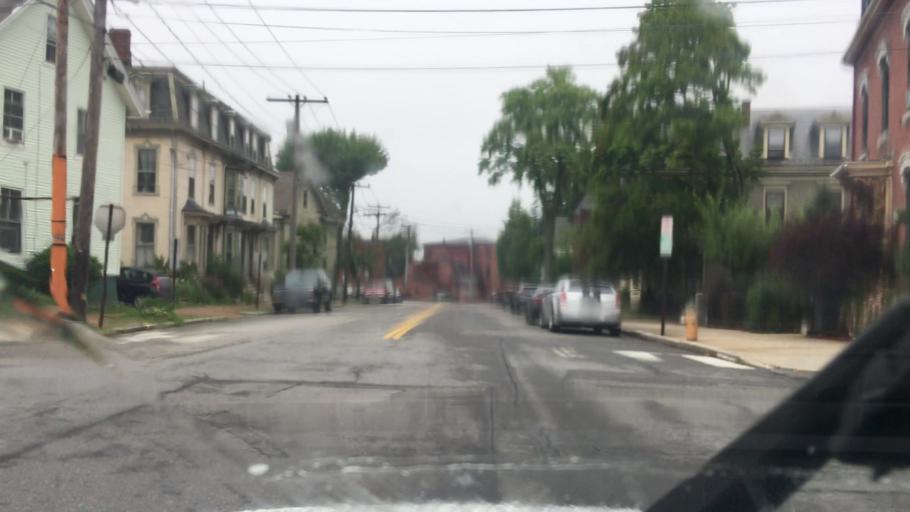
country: US
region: Maine
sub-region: Cumberland County
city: Portland
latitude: 43.6527
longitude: -70.2732
